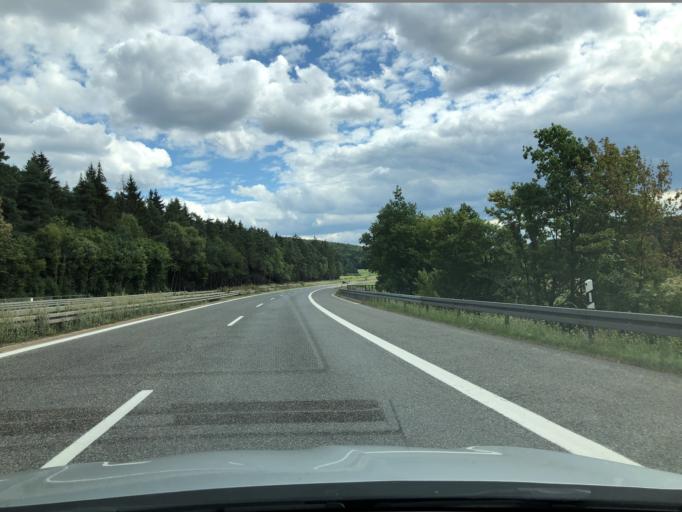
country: DE
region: Bavaria
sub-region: Regierungsbezirk Mittelfranken
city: Alfeld
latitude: 49.4136
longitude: 11.5602
